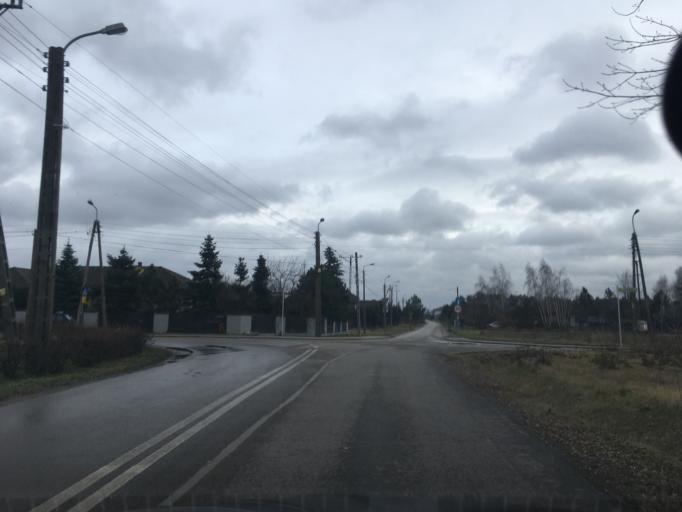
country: PL
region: Masovian Voivodeship
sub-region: Powiat piaseczynski
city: Lesznowola
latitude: 52.1188
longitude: 20.9438
